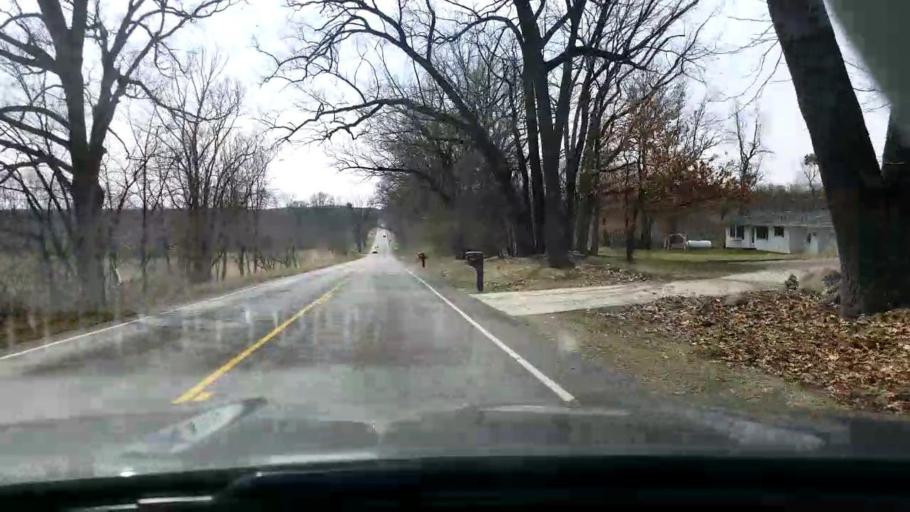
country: US
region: Michigan
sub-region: Jackson County
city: Spring Arbor
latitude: 42.2095
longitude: -84.5212
